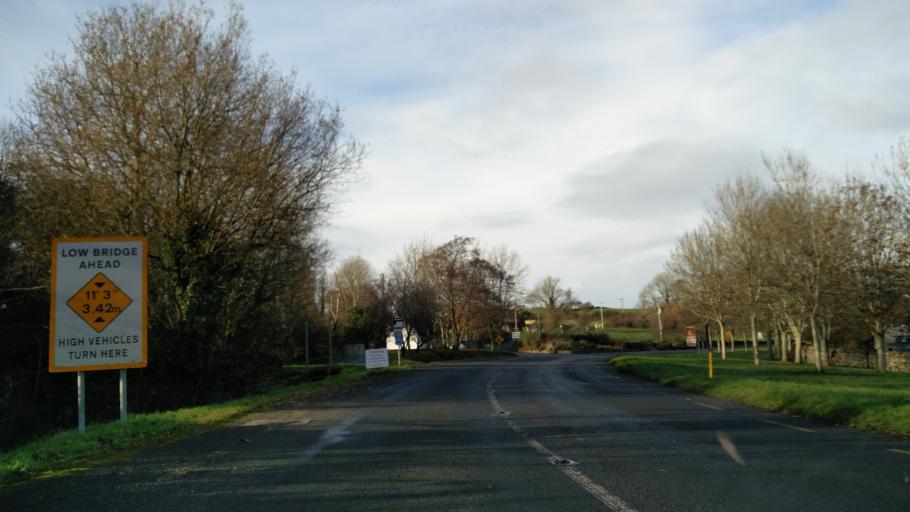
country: IE
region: Connaught
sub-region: Maigh Eo
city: Westport
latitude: 53.7892
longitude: -9.5026
